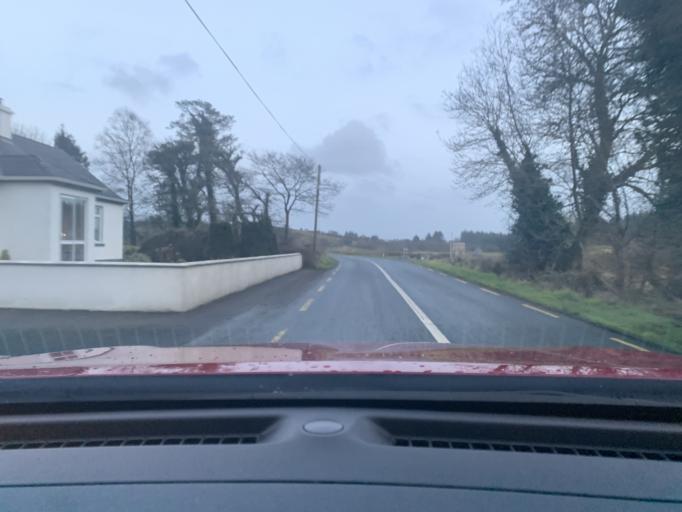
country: IE
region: Connaught
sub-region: Sligo
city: Ballymote
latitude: 54.0398
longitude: -8.4342
